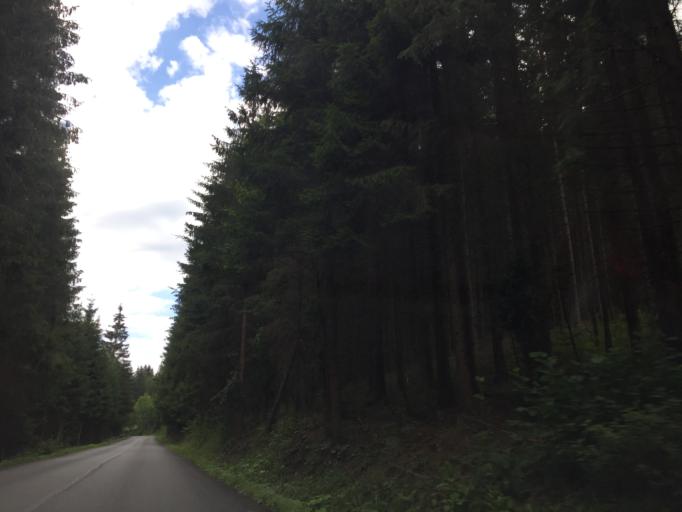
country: SK
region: Zilinsky
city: Namestovo
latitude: 49.4165
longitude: 19.3322
